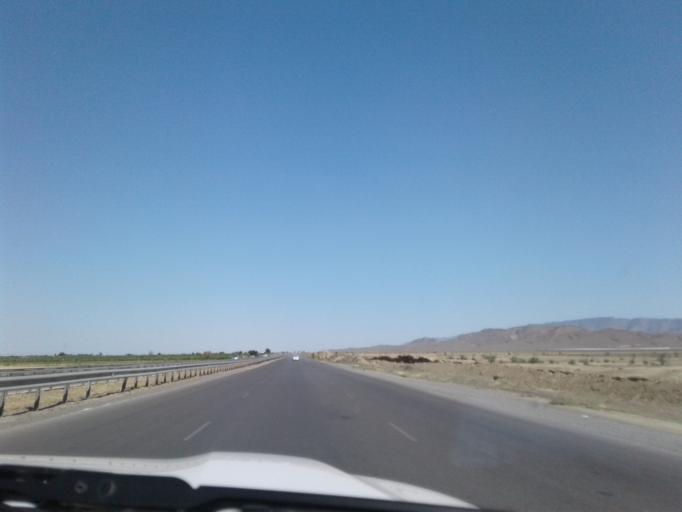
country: TM
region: Ahal
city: Annau
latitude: 37.8016
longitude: 58.7989
